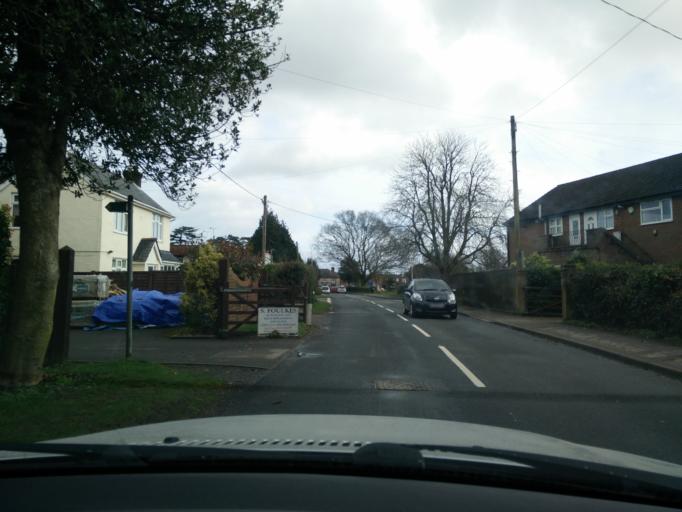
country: GB
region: England
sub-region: Buckinghamshire
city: Great Missenden
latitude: 51.6678
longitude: -0.6938
